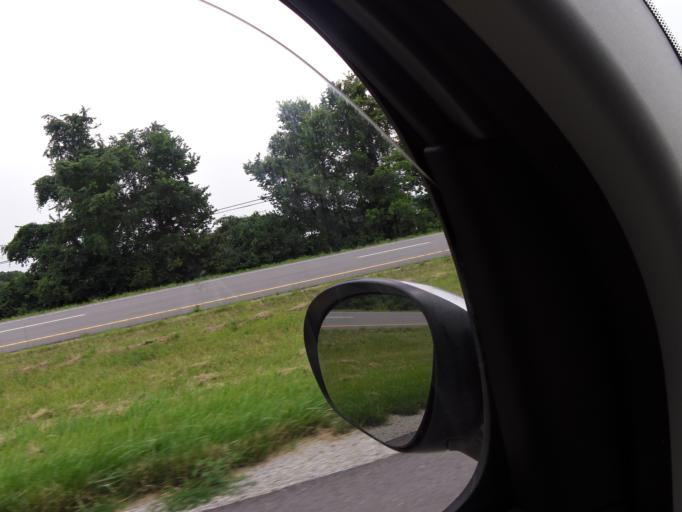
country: US
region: Ohio
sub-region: Warren County
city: Waynesville
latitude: 39.5402
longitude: -84.0666
